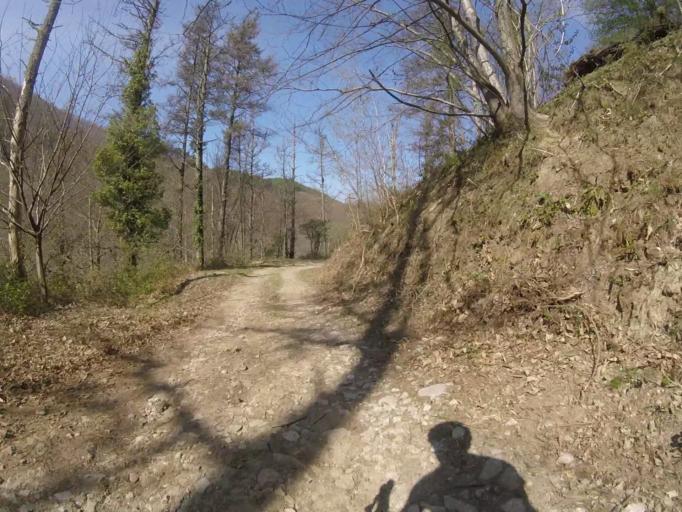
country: ES
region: Basque Country
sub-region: Provincia de Guipuzcoa
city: Irun
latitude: 43.2587
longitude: -1.8085
